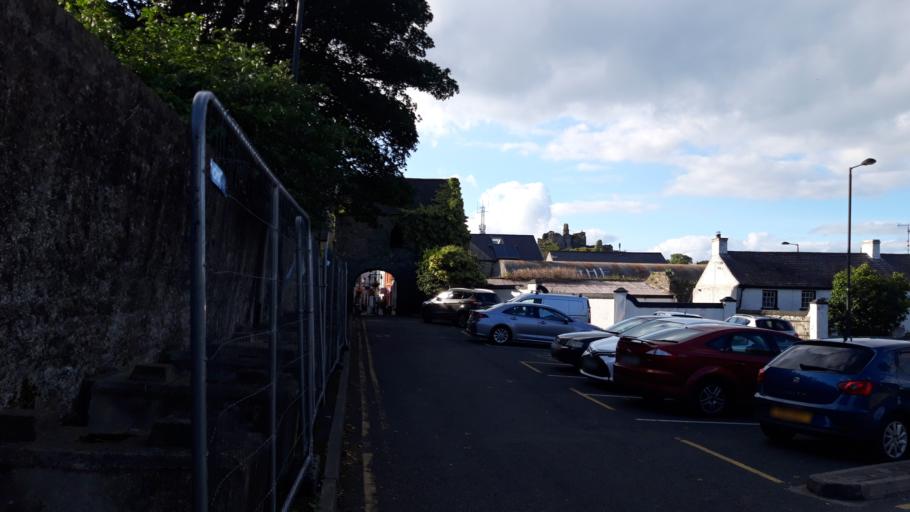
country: IE
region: Leinster
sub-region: Lu
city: Carlingford
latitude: 54.0396
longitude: -6.1850
